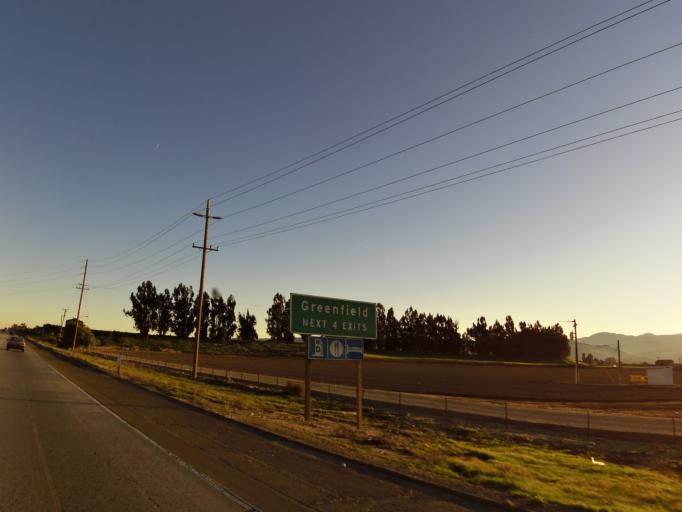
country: US
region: California
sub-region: Monterey County
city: Greenfield
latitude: 36.3499
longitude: -121.2652
